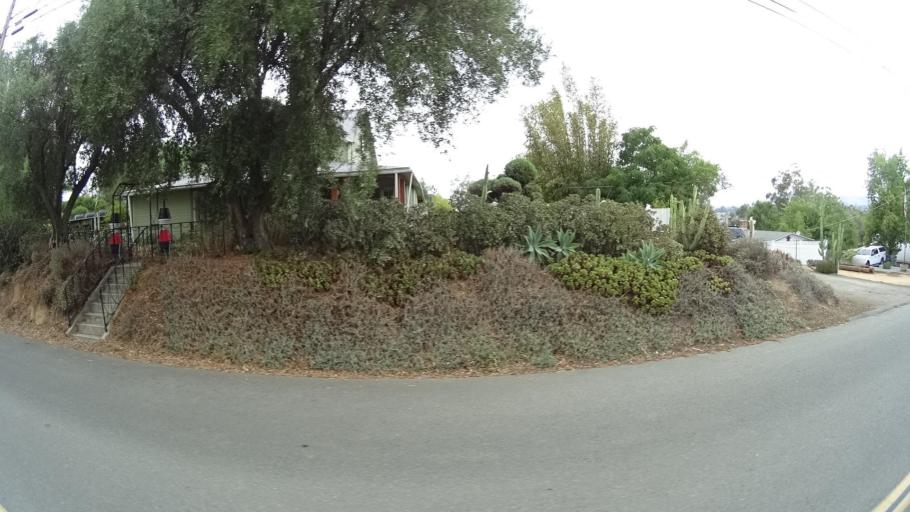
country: US
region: California
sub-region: San Diego County
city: Ramona
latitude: 33.0361
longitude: -116.8595
